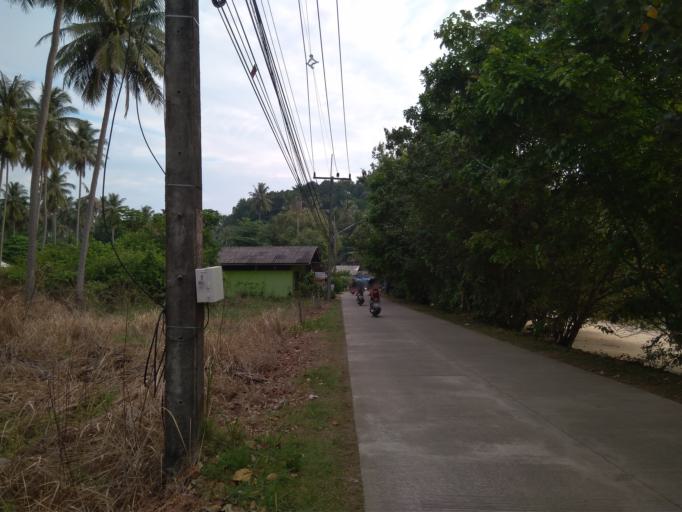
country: TH
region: Phangnga
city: Ko Yao
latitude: 8.1019
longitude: 98.6217
